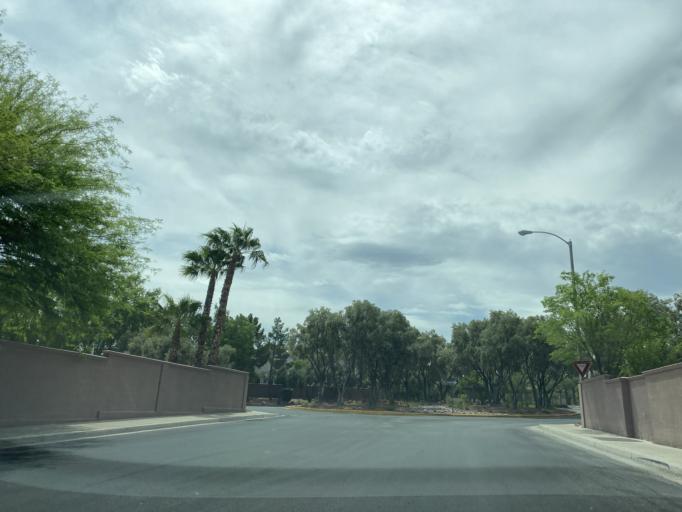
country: US
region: Nevada
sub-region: Clark County
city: Whitney
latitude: 36.0247
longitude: -115.0673
